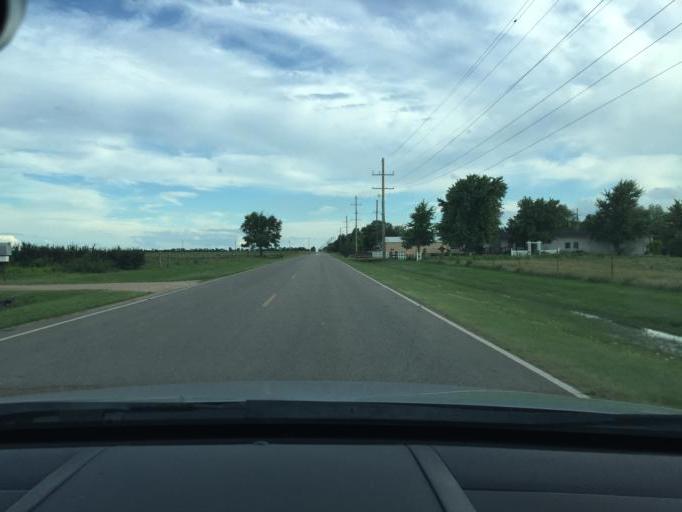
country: US
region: Kansas
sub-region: Reno County
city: Haven
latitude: 37.9314
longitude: -97.8853
